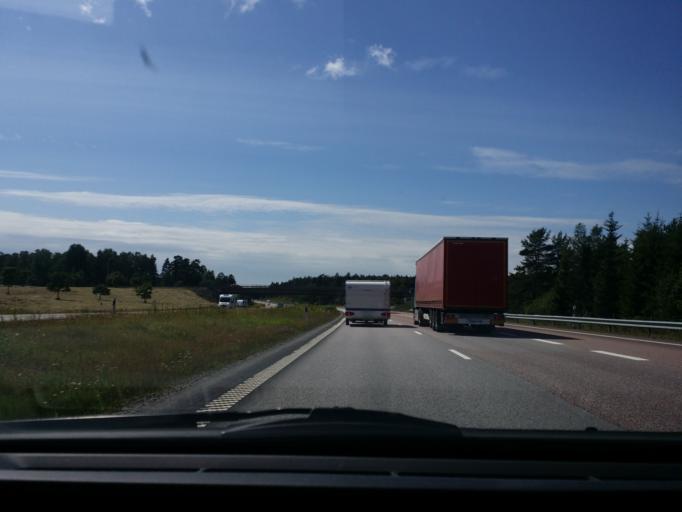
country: SE
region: OErebro
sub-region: Orebro Kommun
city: Orebro
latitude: 59.3053
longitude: 15.2619
